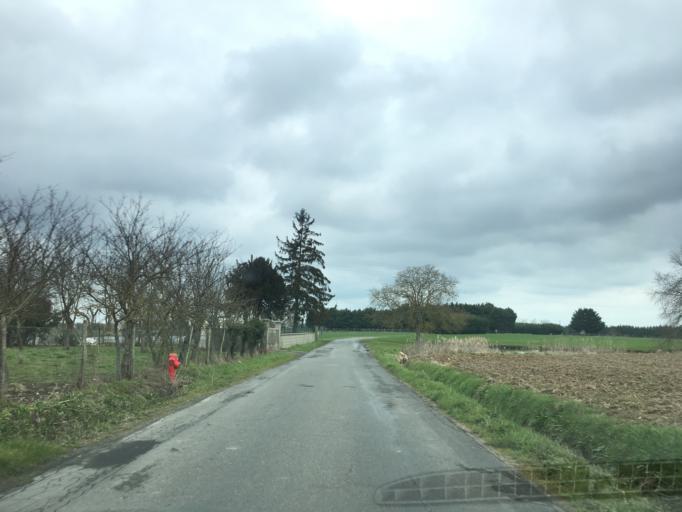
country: FR
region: Centre
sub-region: Departement d'Indre-et-Loire
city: Chanceaux-sur-Choisille
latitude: 47.4686
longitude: 0.6870
